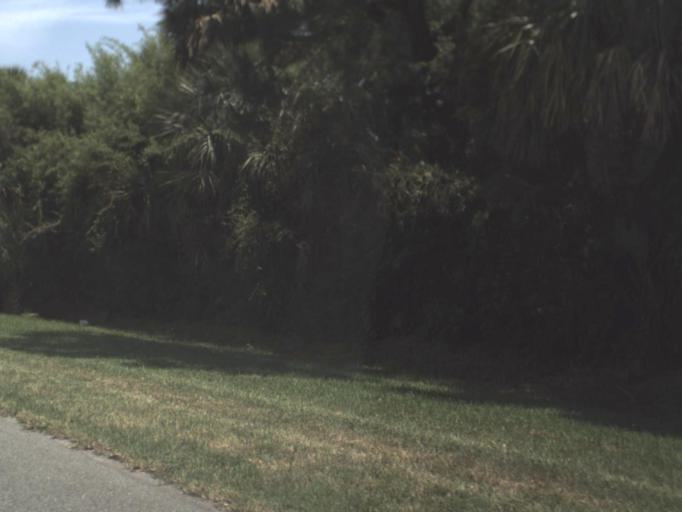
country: US
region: Florida
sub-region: Saint Johns County
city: Ponte Vedra Beach
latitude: 30.2405
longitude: -81.3870
